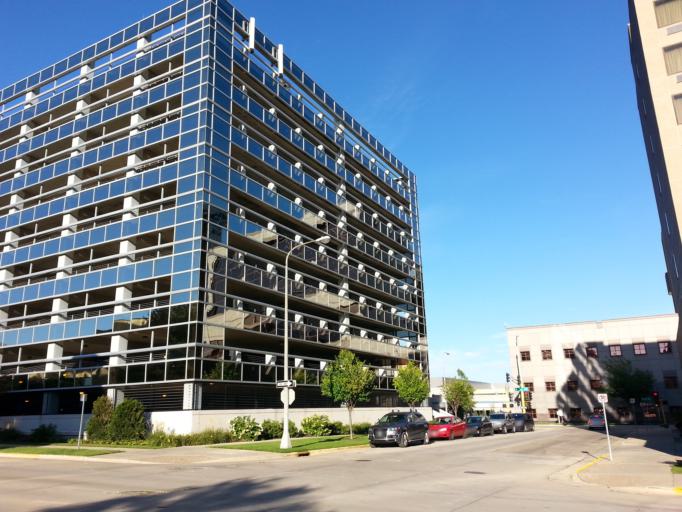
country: US
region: Minnesota
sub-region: Olmsted County
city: Rochester
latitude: 44.0242
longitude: -92.4683
